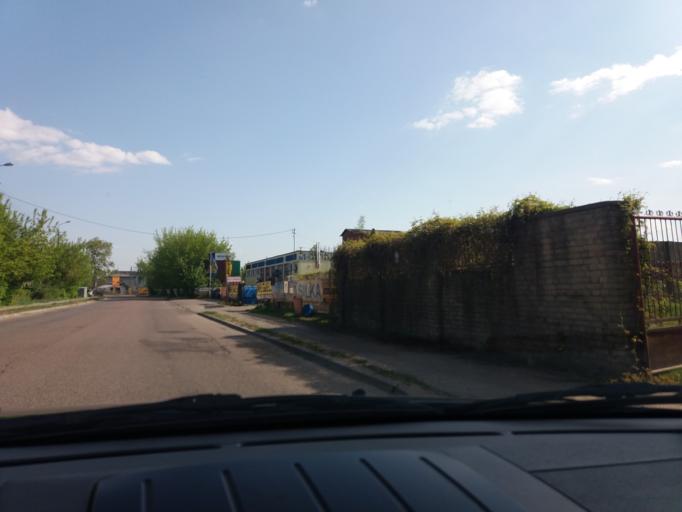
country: PL
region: Masovian Voivodeship
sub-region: Powiat mlawski
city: Mlawa
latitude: 53.1232
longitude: 20.3546
